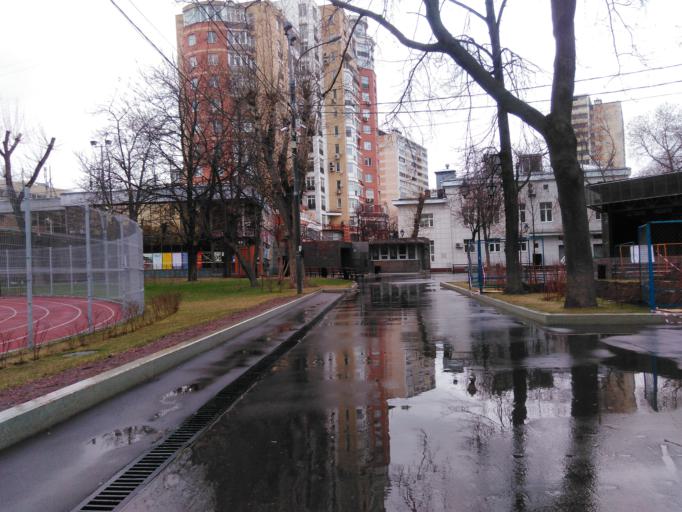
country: RU
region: Moscow
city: Taganskiy
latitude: 55.7380
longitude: 37.6674
